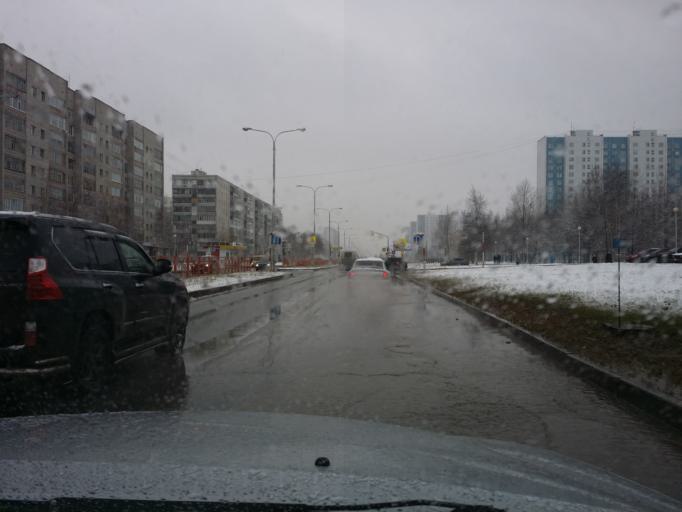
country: RU
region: Khanty-Mansiyskiy Avtonomnyy Okrug
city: Nizhnevartovsk
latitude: 60.9437
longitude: 76.6001
